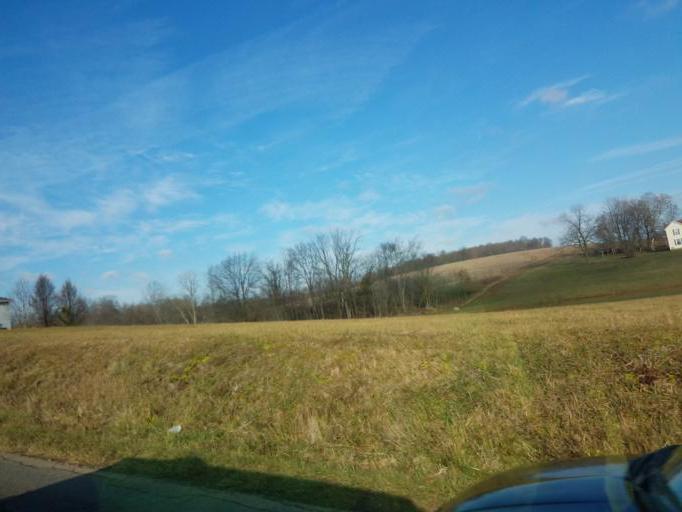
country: US
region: Ohio
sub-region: Knox County
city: Danville
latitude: 40.4514
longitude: -82.2678
